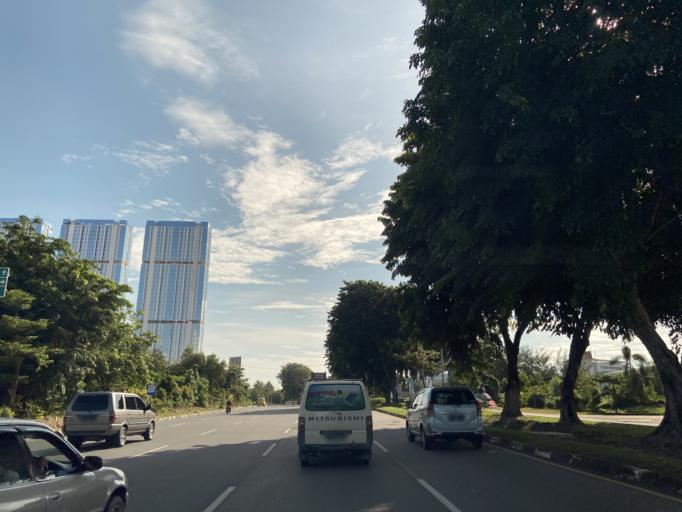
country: SG
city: Singapore
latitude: 1.1162
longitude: 104.0449
